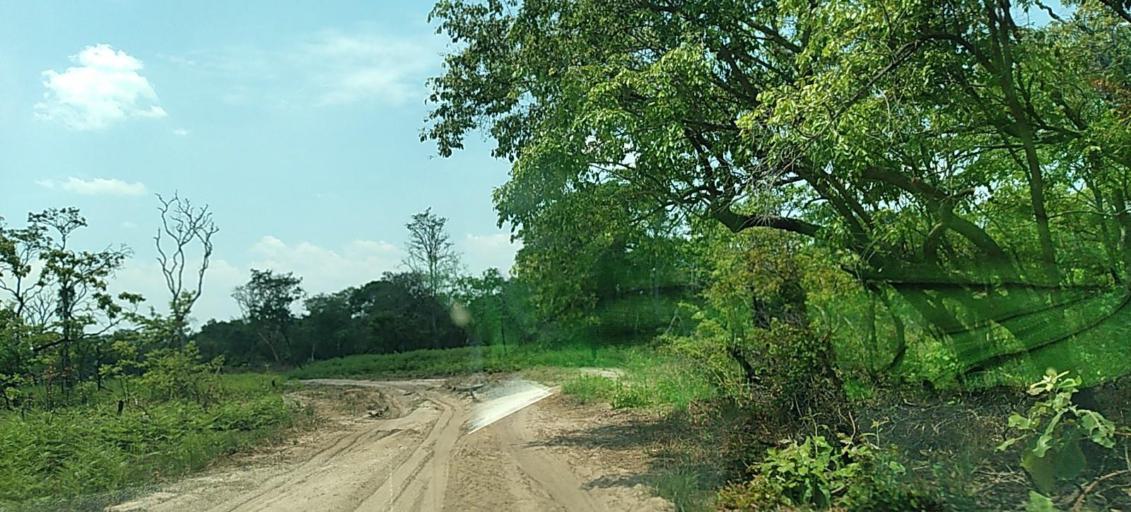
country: CD
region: Katanga
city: Kolwezi
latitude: -11.3135
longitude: 25.2359
